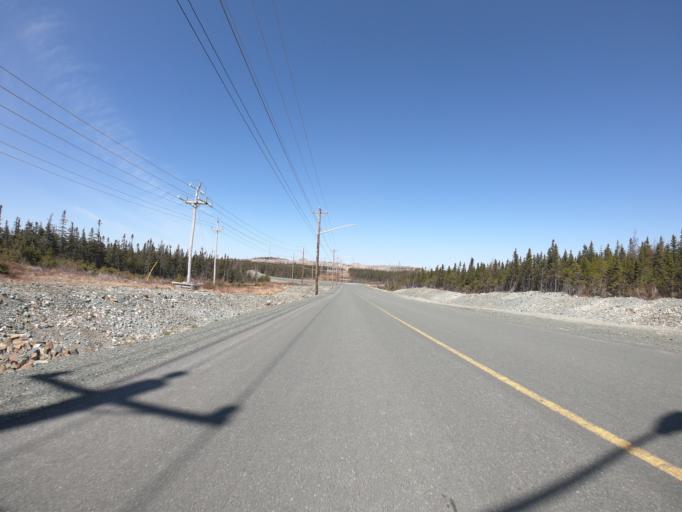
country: CA
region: Newfoundland and Labrador
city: Mount Pearl
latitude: 47.5038
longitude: -52.8500
